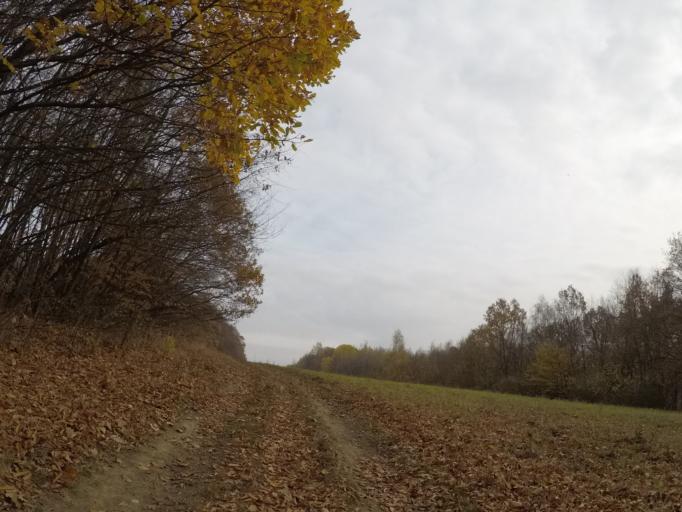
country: SK
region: Presovsky
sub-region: Okres Presov
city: Presov
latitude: 48.9411
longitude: 21.1436
